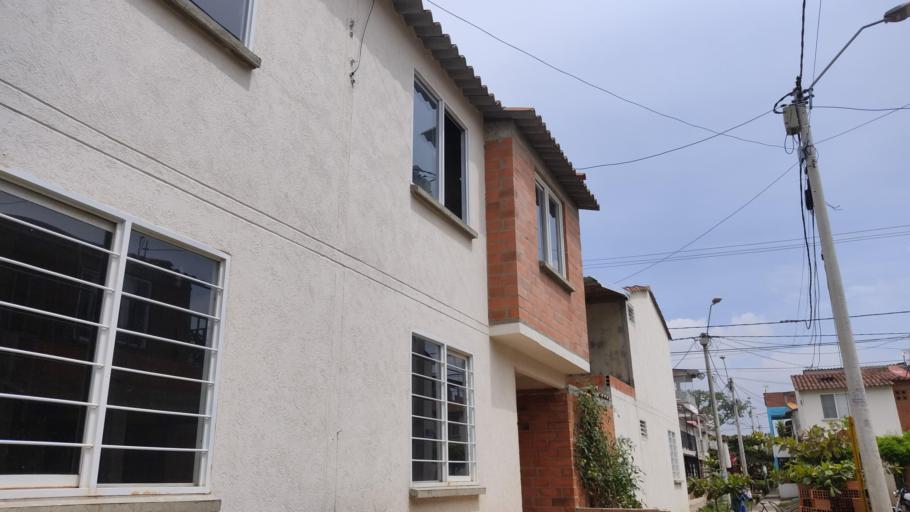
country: CO
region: Valle del Cauca
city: Jamundi
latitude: 3.2360
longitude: -76.5116
